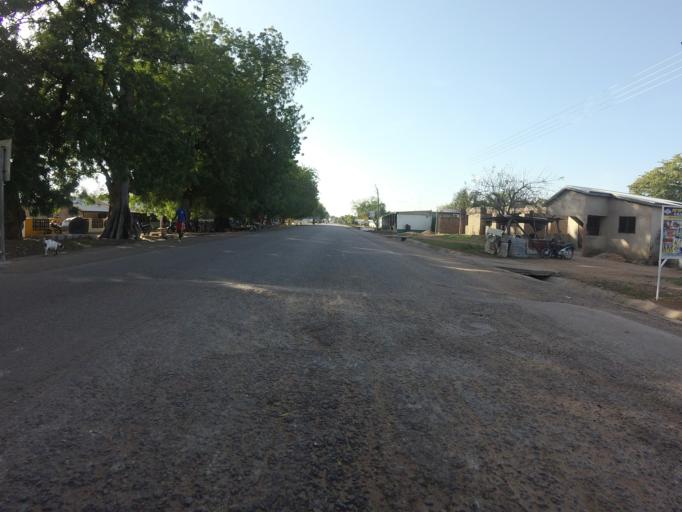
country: GH
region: Upper East
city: Navrongo
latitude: 10.9676
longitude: -1.1016
